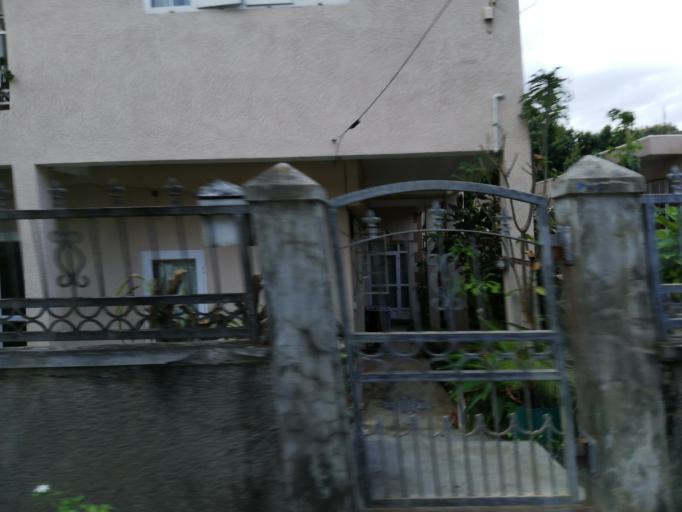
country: MU
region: Plaines Wilhems
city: Ebene
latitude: -20.2323
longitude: 57.4582
